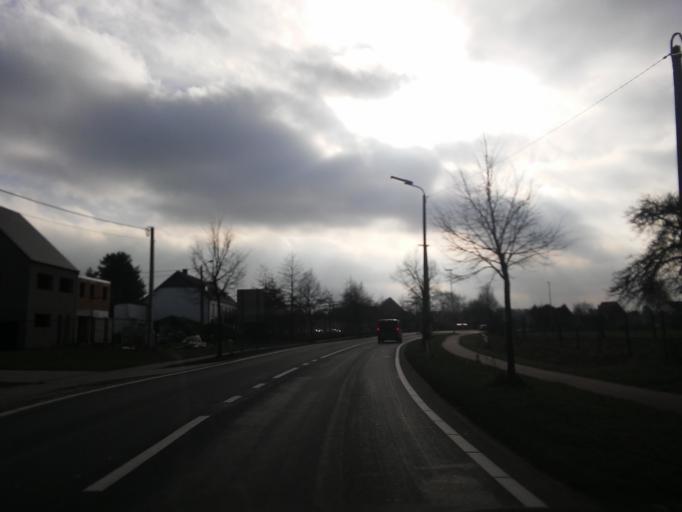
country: BE
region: Flanders
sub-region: Provincie Antwerpen
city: Herselt
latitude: 51.0929
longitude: 4.8705
